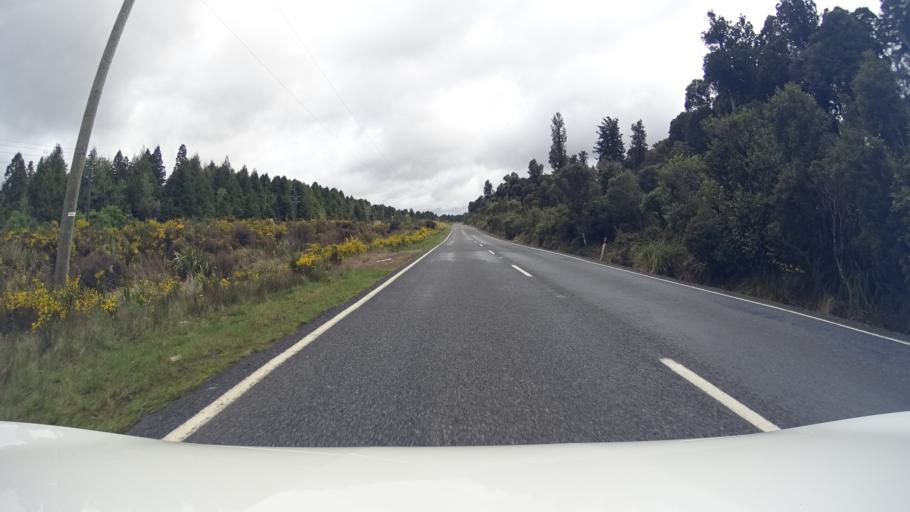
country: NZ
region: Manawatu-Wanganui
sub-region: Ruapehu District
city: Waiouru
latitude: -39.2526
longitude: 175.3881
